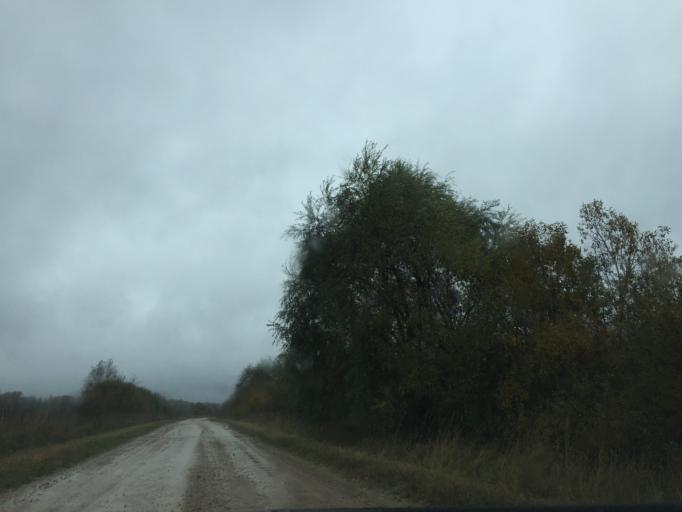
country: LV
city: Tireli
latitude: 56.7706
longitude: 23.5431
